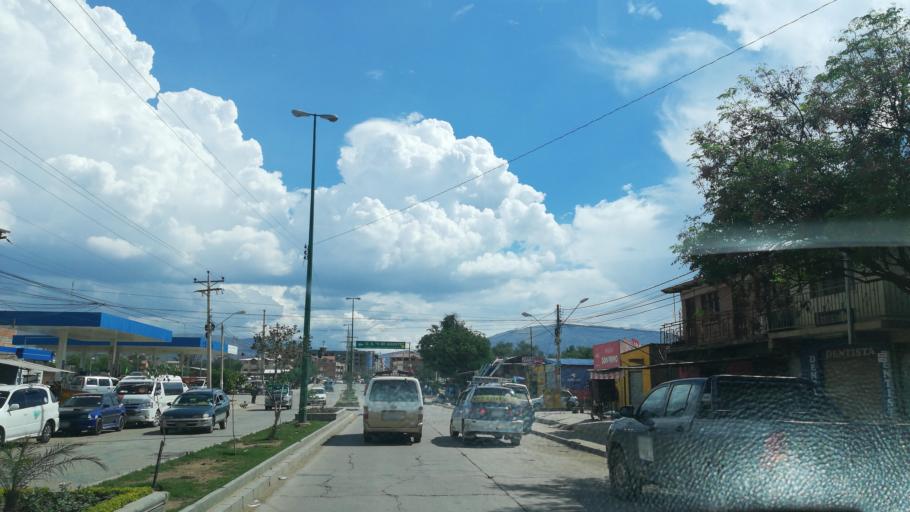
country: BO
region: Cochabamba
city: Cochabamba
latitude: -17.4361
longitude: -66.1653
